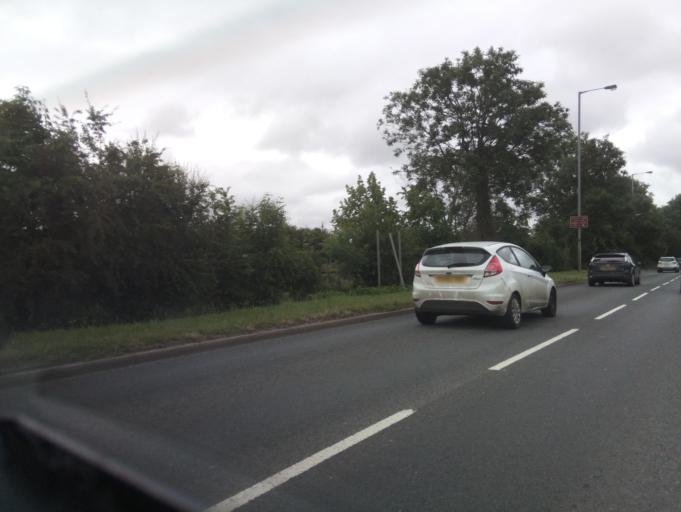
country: GB
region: England
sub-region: Staffordshire
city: Burton upon Trent
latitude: 52.8313
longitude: -1.6141
